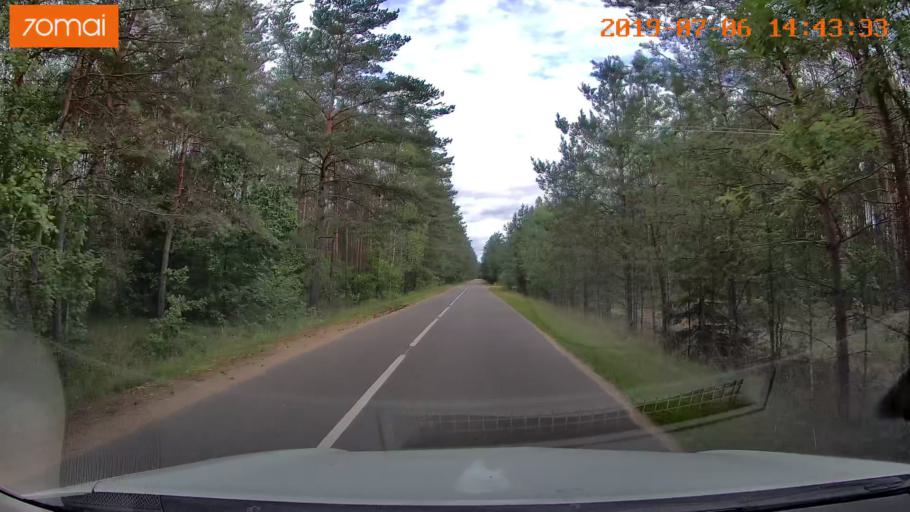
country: BY
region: Minsk
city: Ivyanyets
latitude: 53.9534
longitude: 26.6940
